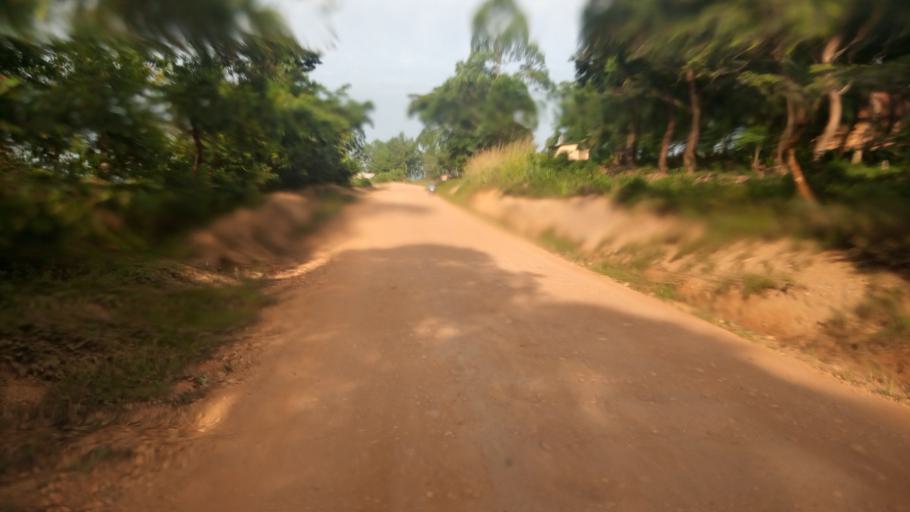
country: UG
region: Western Region
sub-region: Kanungu District
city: Ntungamo
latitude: -0.8350
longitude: 29.6714
